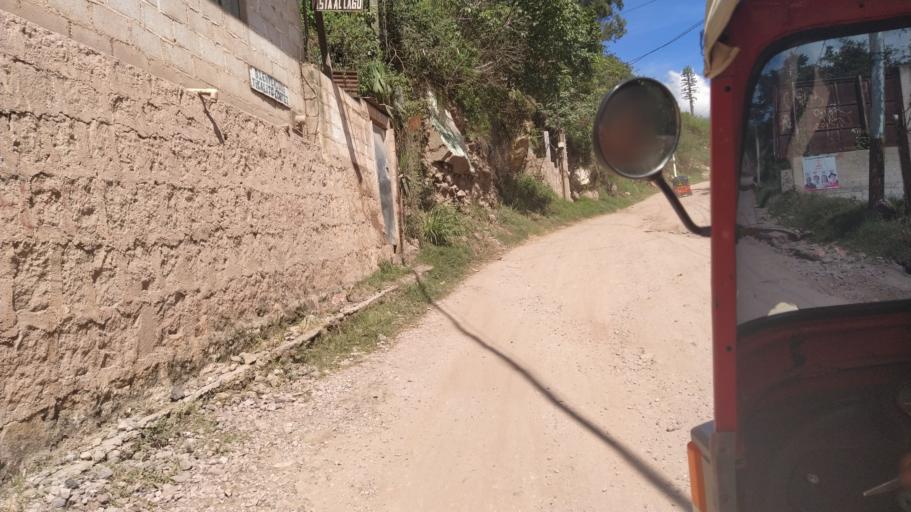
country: GT
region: Solola
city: San Pedro La Laguna
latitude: 14.6935
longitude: -91.2777
